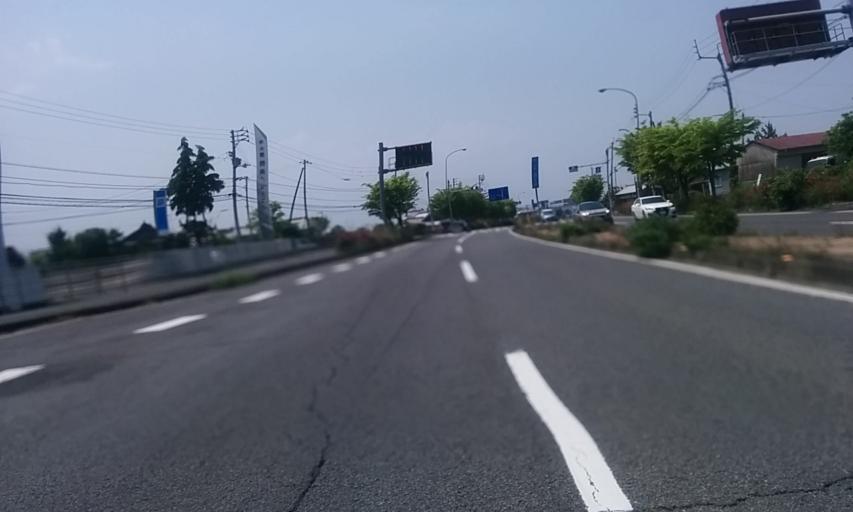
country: JP
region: Ehime
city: Saijo
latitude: 33.9196
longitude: 133.2393
